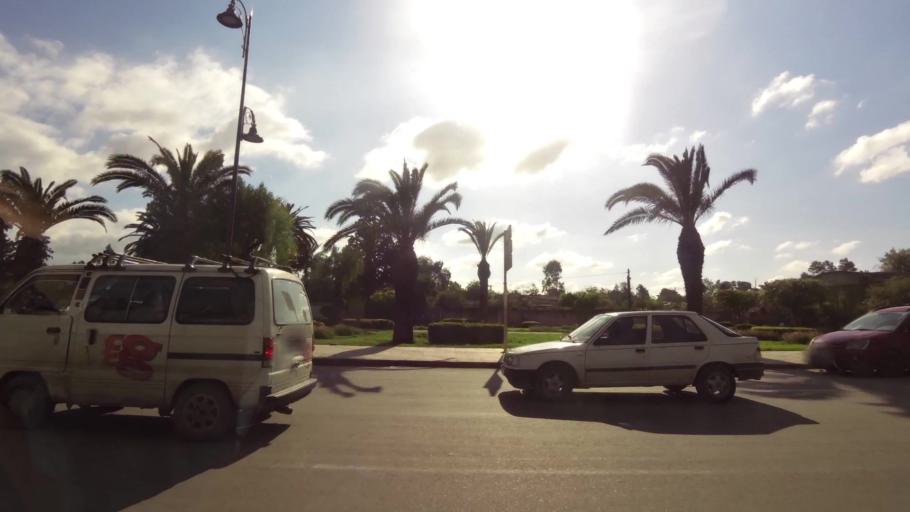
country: MA
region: Chaouia-Ouardigha
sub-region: Settat Province
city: Berrechid
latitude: 33.2622
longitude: -7.5819
